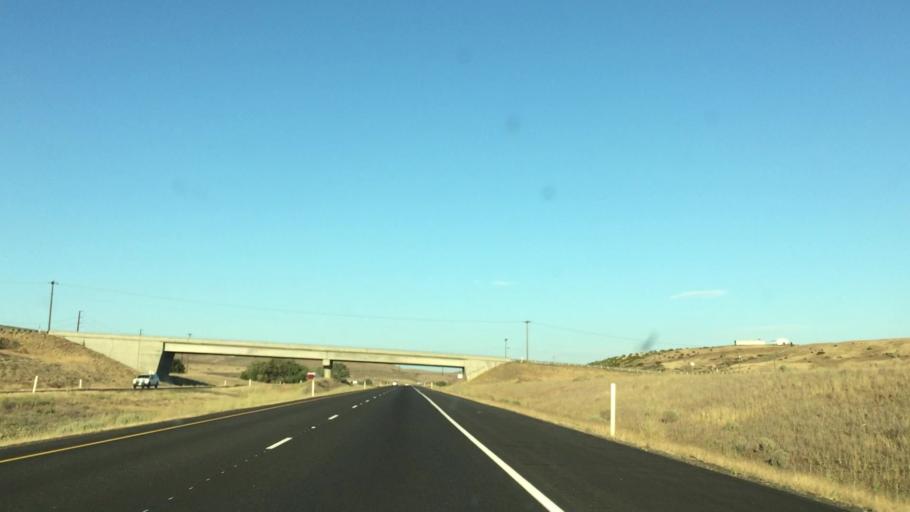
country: US
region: Washington
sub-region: Kittitas County
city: Kittitas
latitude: 46.9728
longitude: -120.3672
